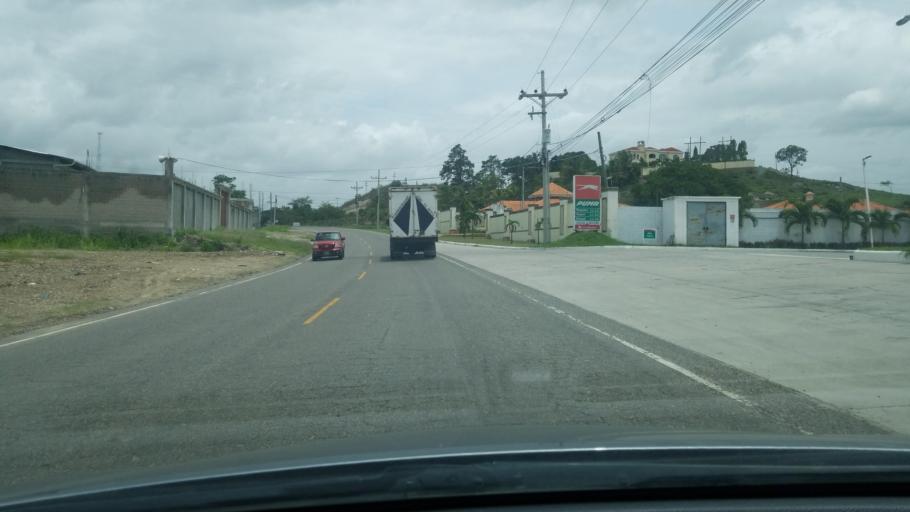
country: HN
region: Copan
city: Cucuyagua
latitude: 14.6638
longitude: -88.8708
